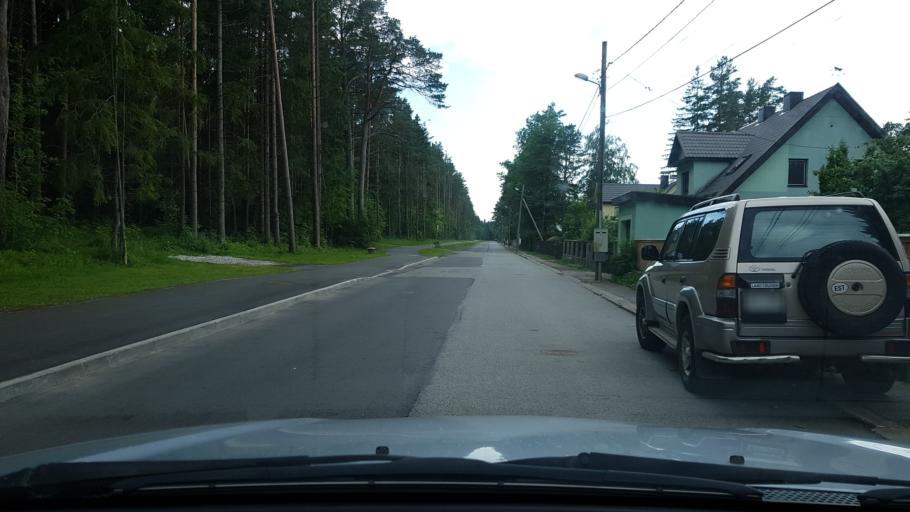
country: EE
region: Ida-Virumaa
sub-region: Narva-Joesuu linn
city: Narva-Joesuu
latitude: 59.4520
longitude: 28.0329
